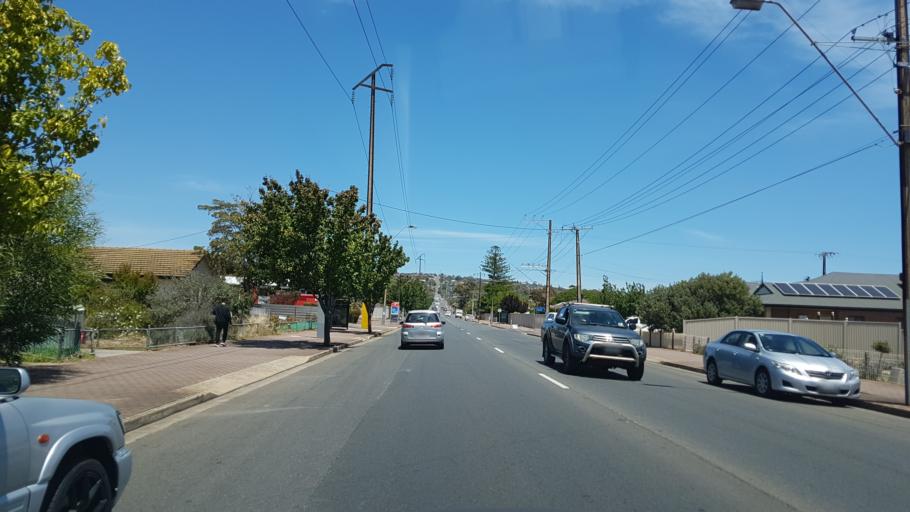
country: AU
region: South Australia
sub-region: Marion
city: Sturt
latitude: -35.0213
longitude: 138.5412
